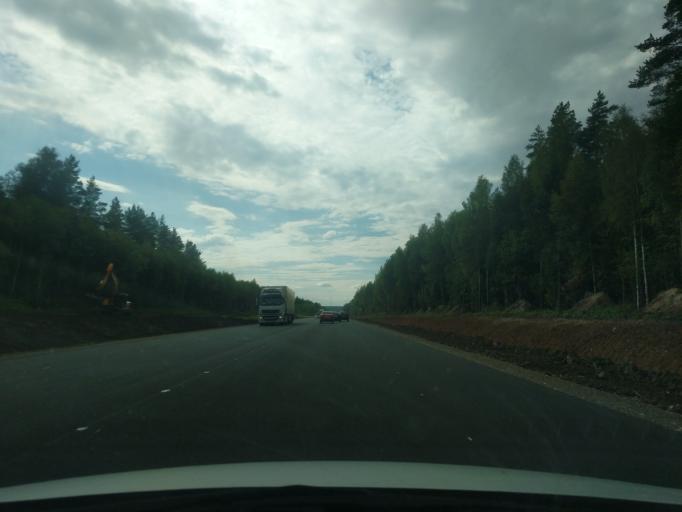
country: RU
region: Kostroma
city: Sudislavl'
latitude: 57.8241
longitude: 41.4973
